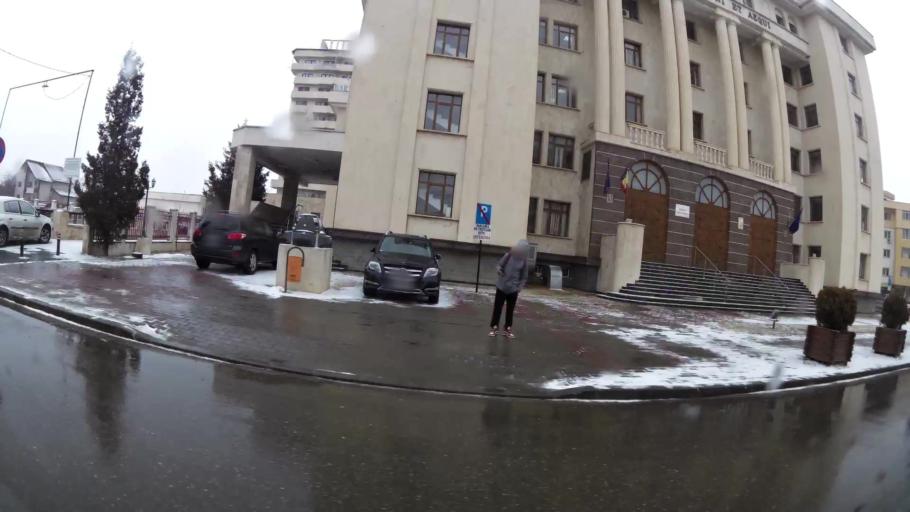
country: RO
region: Dambovita
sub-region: Municipiul Targoviste
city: Targoviste
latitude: 44.9209
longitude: 25.4761
